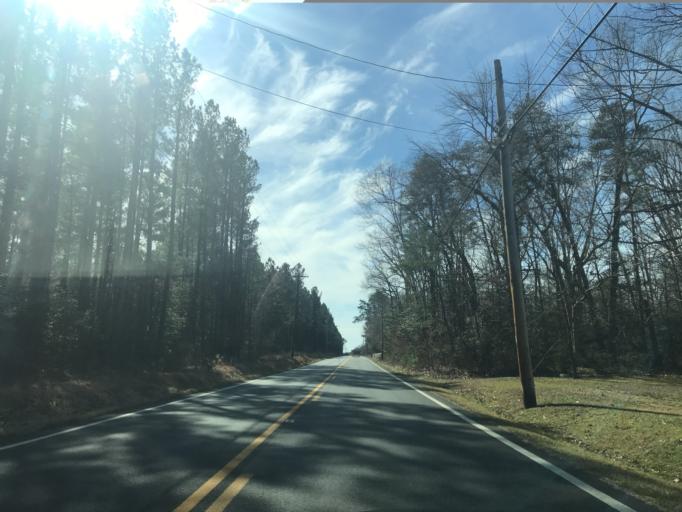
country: US
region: Maryland
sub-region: Charles County
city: Indian Head
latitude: 38.5341
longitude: -77.1383
